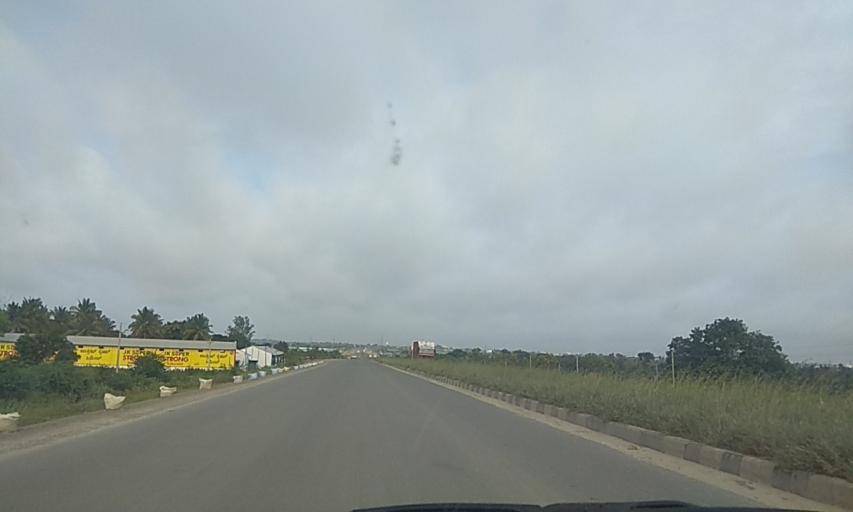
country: IN
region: Karnataka
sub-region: Haveri
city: Haveri
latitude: 14.7739
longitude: 75.4075
